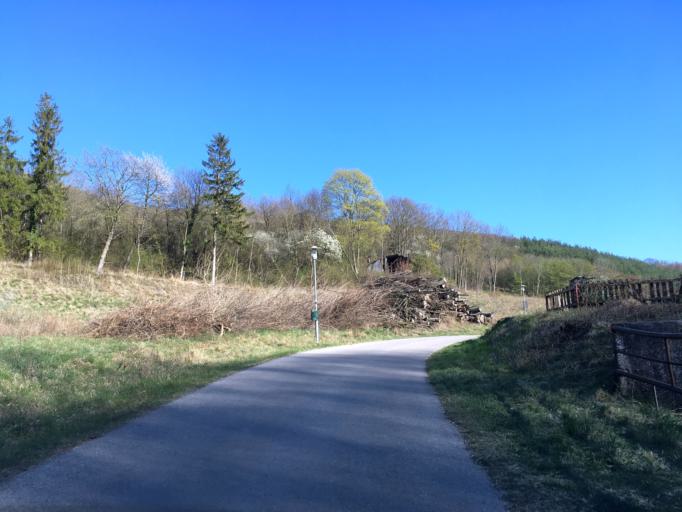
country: AT
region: Lower Austria
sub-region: Politischer Bezirk Tulln
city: Konigstetten
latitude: 48.2948
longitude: 16.1543
